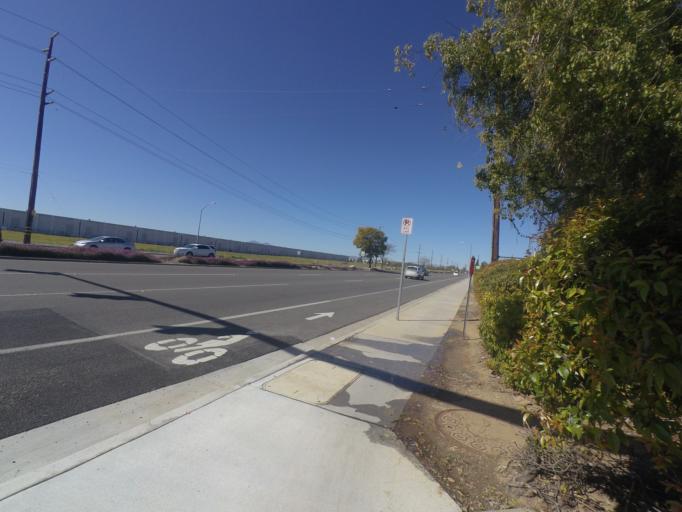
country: US
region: California
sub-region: Riverside County
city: March Air Force Base
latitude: 33.9174
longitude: -117.2526
